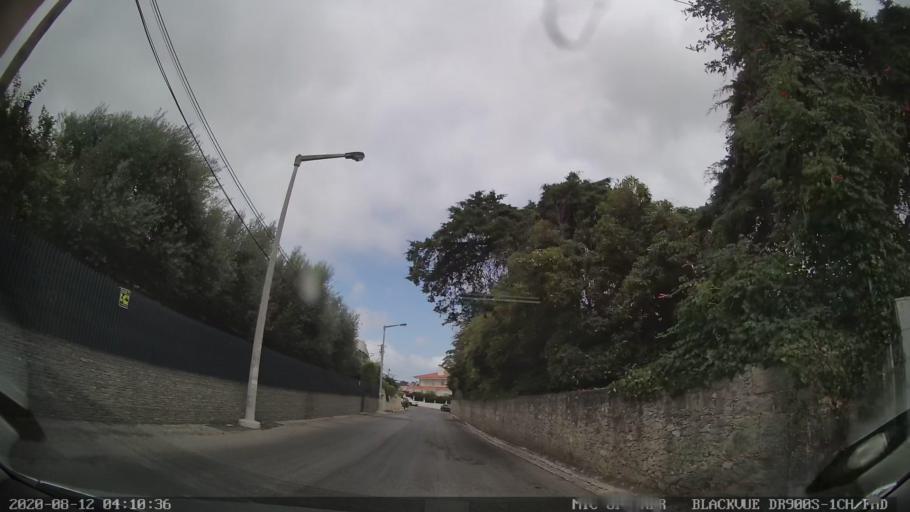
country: PT
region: Lisbon
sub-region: Cascais
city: Estoril
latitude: 38.7039
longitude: -9.3754
